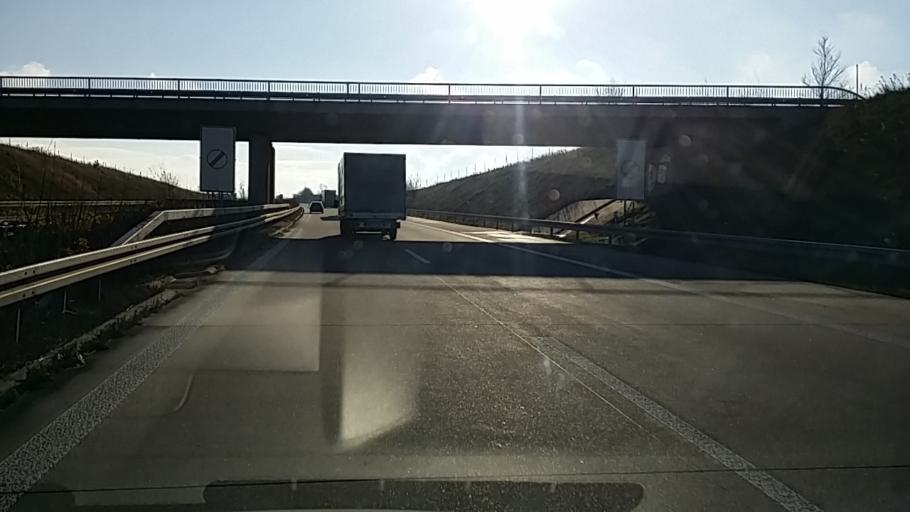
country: DE
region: Saxony
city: Liebstadt
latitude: 50.8627
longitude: 13.8724
